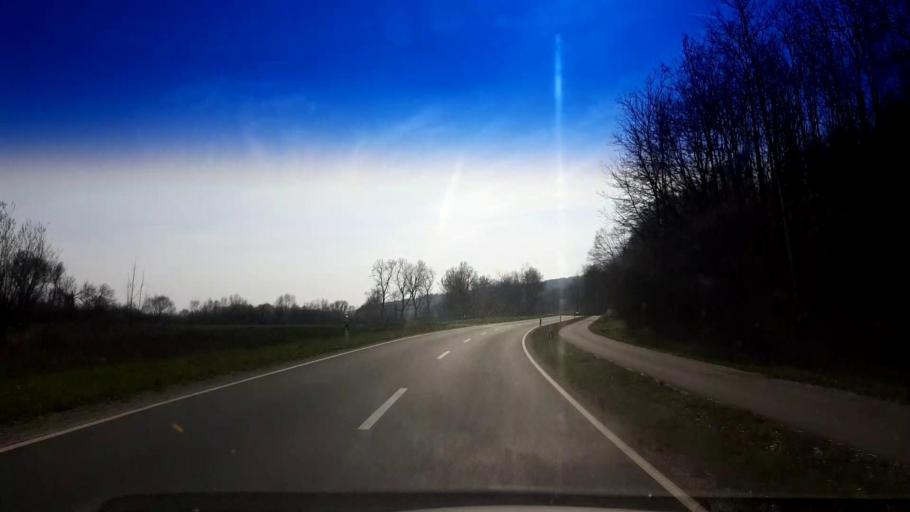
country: DE
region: Bavaria
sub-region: Upper Franconia
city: Ebensfeld
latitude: 50.0595
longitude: 10.9396
